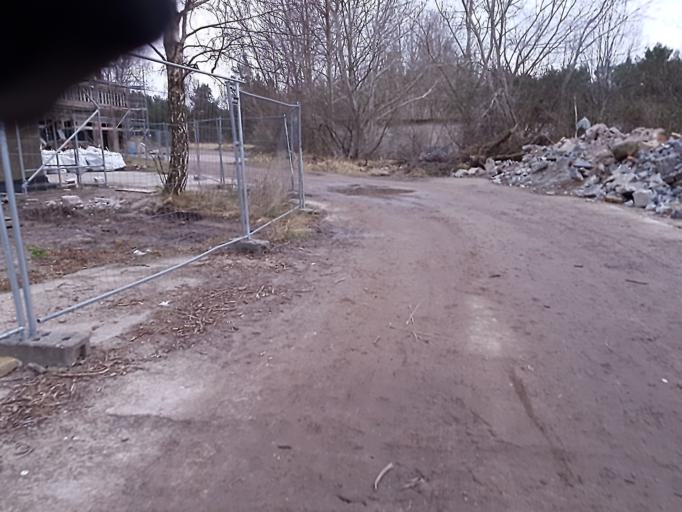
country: DE
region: Mecklenburg-Vorpommern
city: Ostseebad Binz
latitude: 54.4434
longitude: 13.5726
